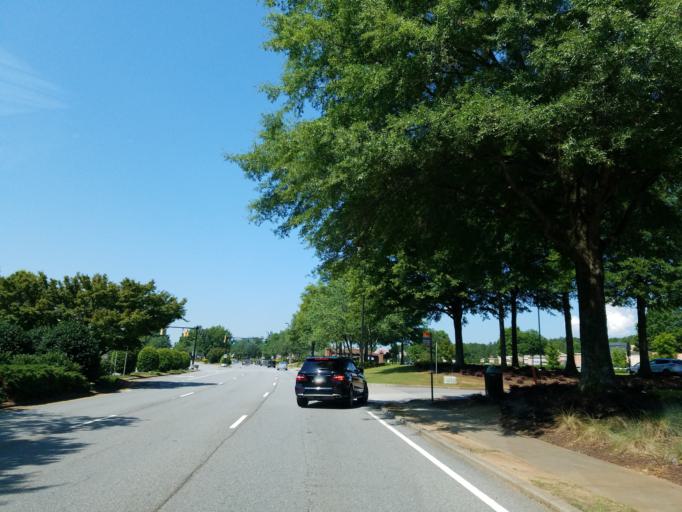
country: US
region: Georgia
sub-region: Fulton County
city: Alpharetta
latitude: 34.0426
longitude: -84.3030
